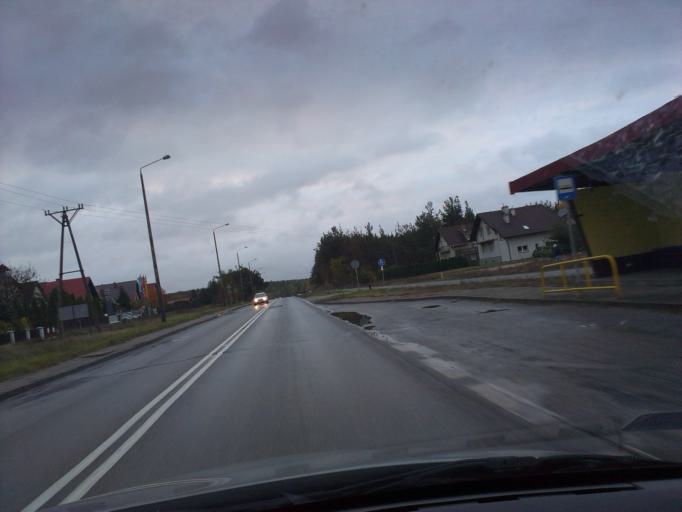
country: PL
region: Kujawsko-Pomorskie
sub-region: Powiat tucholski
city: Tuchola
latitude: 53.5690
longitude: 17.8913
